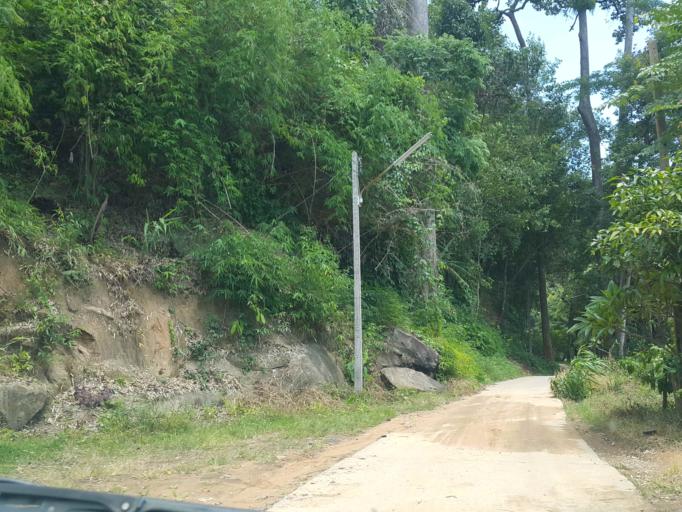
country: TH
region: Chiang Mai
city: Chom Thong
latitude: 18.5438
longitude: 98.5927
